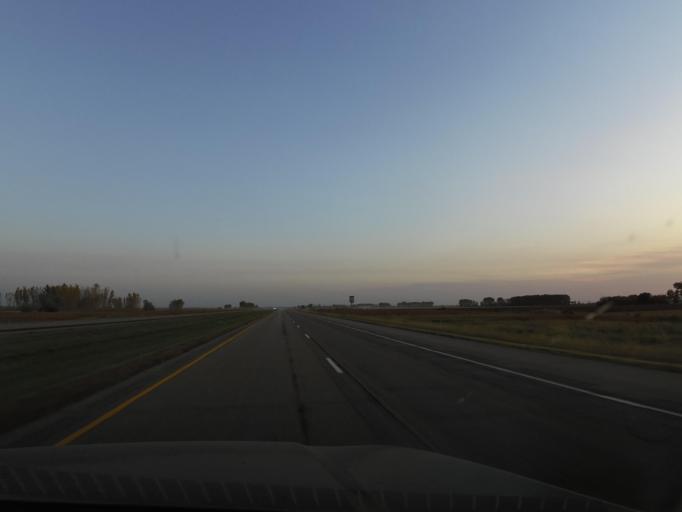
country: US
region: Minnesota
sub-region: Kittson County
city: Hallock
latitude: 48.6523
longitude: -97.1822
